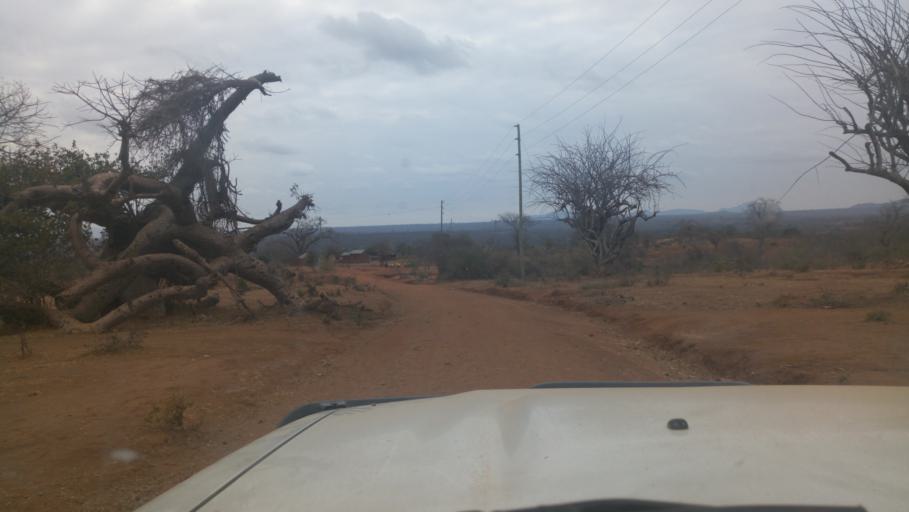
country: KE
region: Makueni
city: Makueni
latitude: -2.0133
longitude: 38.1088
